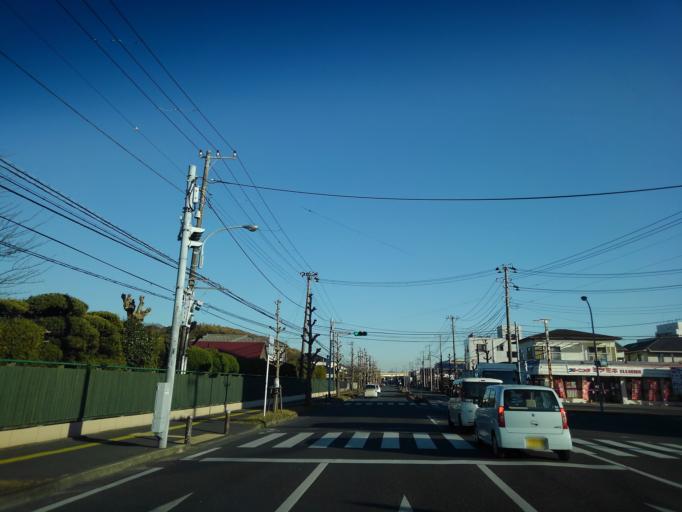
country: JP
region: Chiba
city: Kimitsu
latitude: 35.3337
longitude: 139.8990
